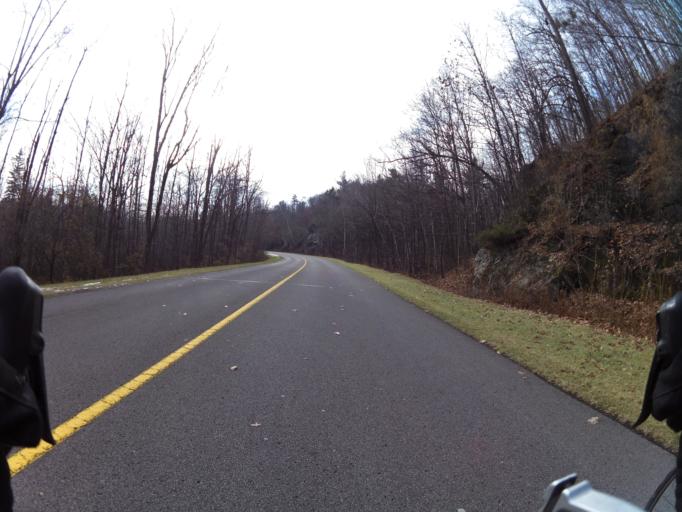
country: CA
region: Quebec
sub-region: Outaouais
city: Gatineau
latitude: 45.4618
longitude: -75.7908
